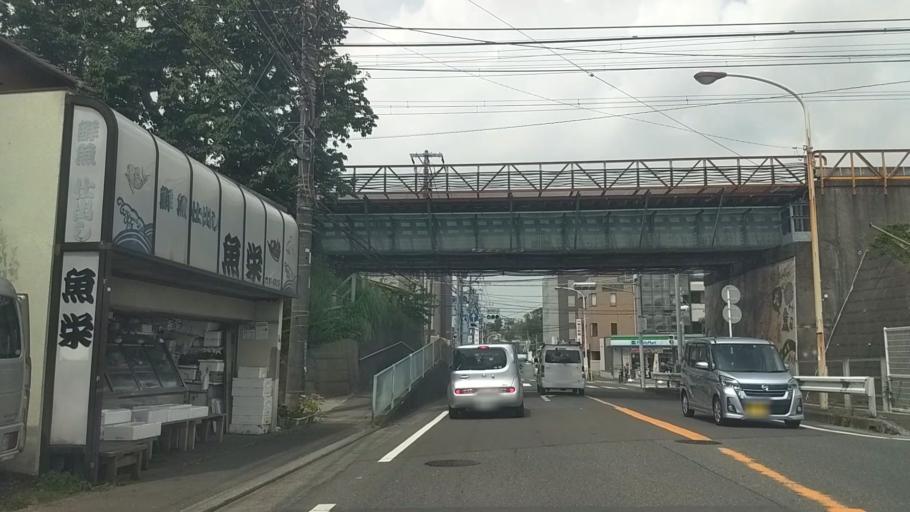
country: JP
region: Kanagawa
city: Fujisawa
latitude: 35.3644
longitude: 139.4734
